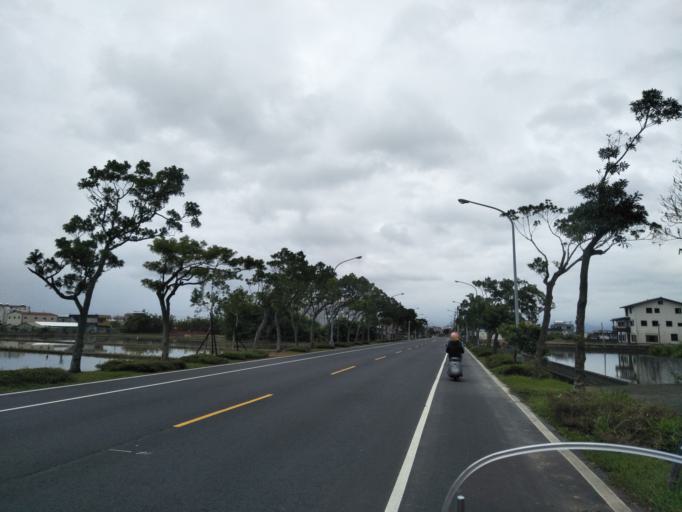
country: TW
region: Taiwan
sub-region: Yilan
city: Yilan
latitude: 24.7790
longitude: 121.7832
